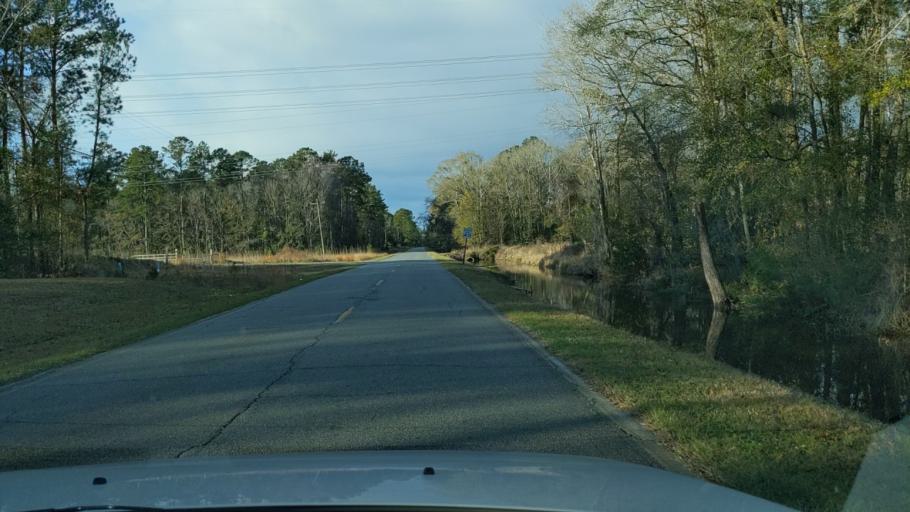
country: US
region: Georgia
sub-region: Chatham County
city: Georgetown
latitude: 32.0387
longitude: -81.3004
